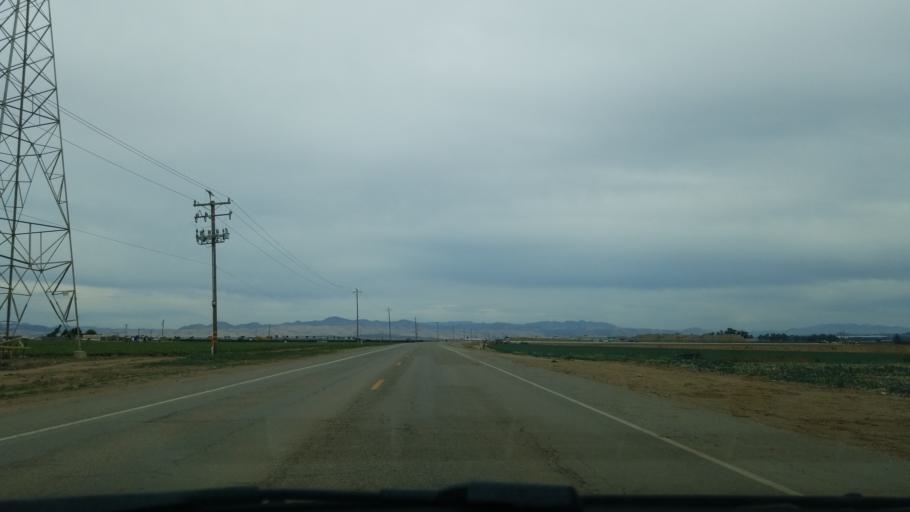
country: US
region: California
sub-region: Santa Barbara County
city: Santa Maria
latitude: 34.9199
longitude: -120.5031
